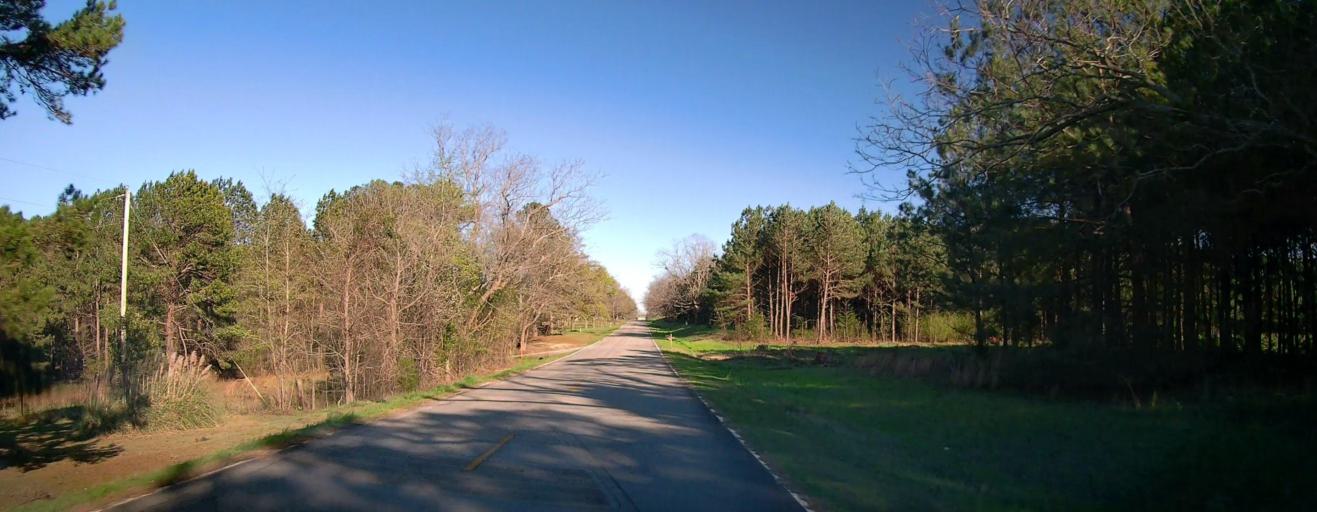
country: US
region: Georgia
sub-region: Houston County
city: Perry
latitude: 32.3744
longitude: -83.7166
